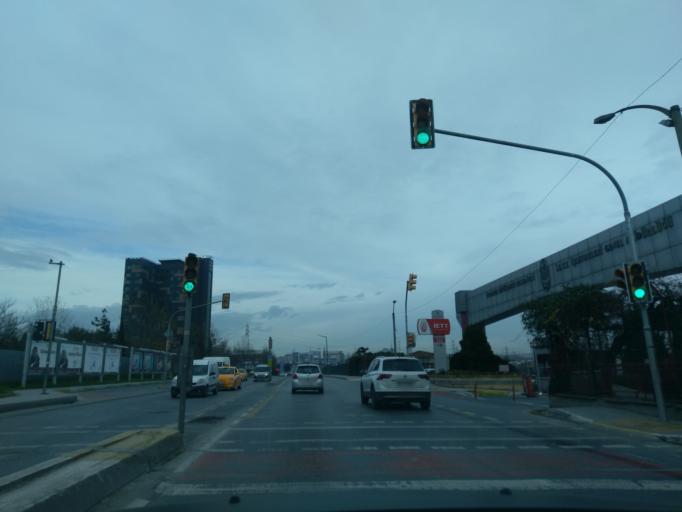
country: TR
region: Istanbul
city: Mahmutbey
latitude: 41.0582
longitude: 28.7912
